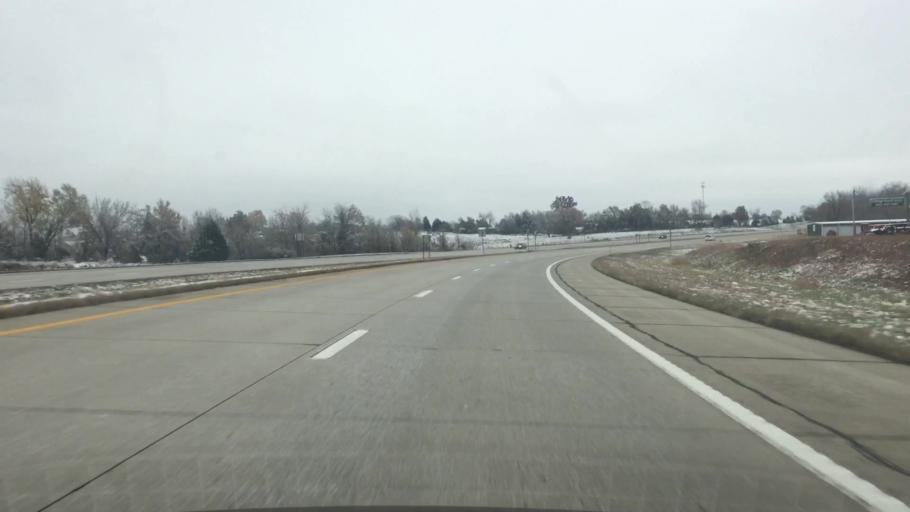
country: US
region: Missouri
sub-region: Saint Clair County
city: Osceola
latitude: 38.1772
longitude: -93.7235
